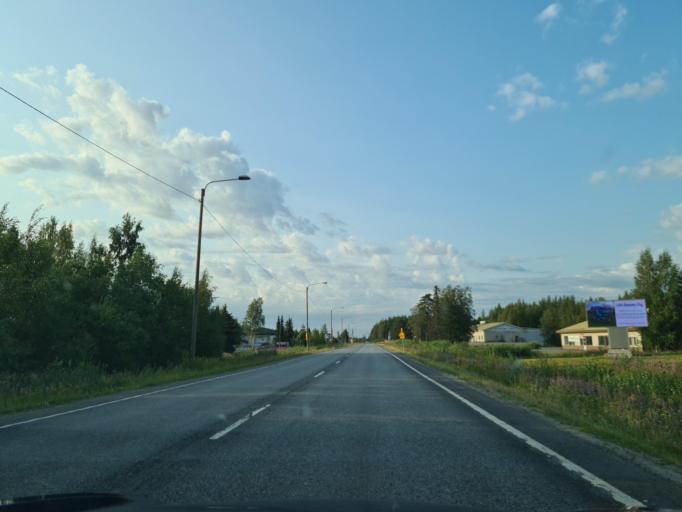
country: FI
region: Southern Ostrobothnia
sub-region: Seinaejoki
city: Kauhava
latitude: 63.0804
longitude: 23.0583
